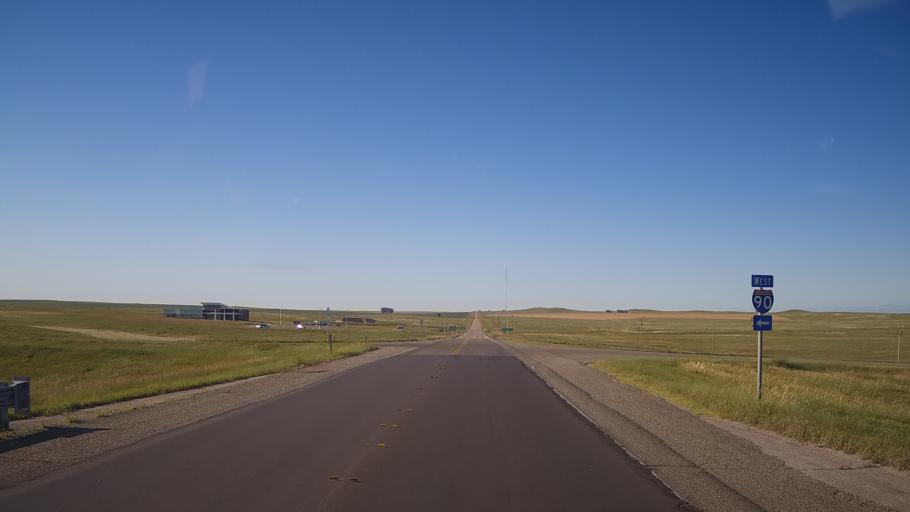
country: US
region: South Dakota
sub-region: Haakon County
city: Philip
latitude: 43.8410
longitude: -101.8996
